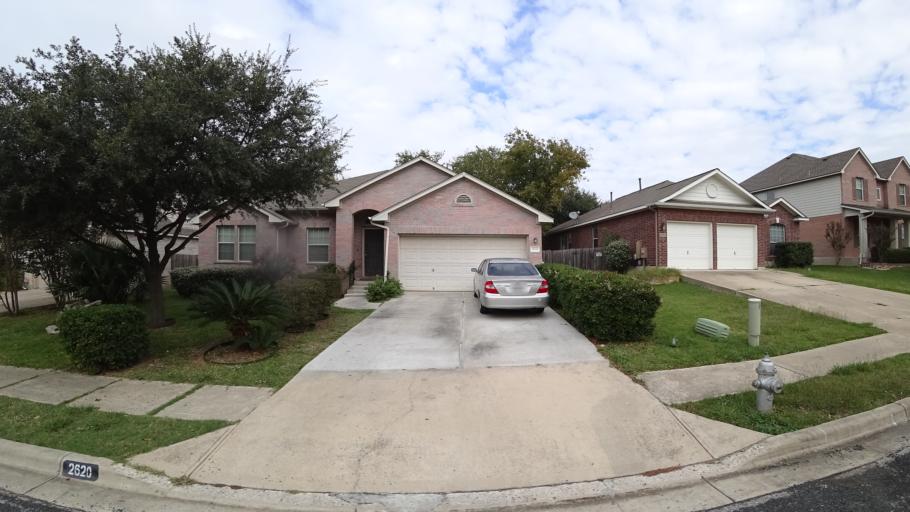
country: US
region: Texas
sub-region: Travis County
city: Wells Branch
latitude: 30.4327
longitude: -97.6933
